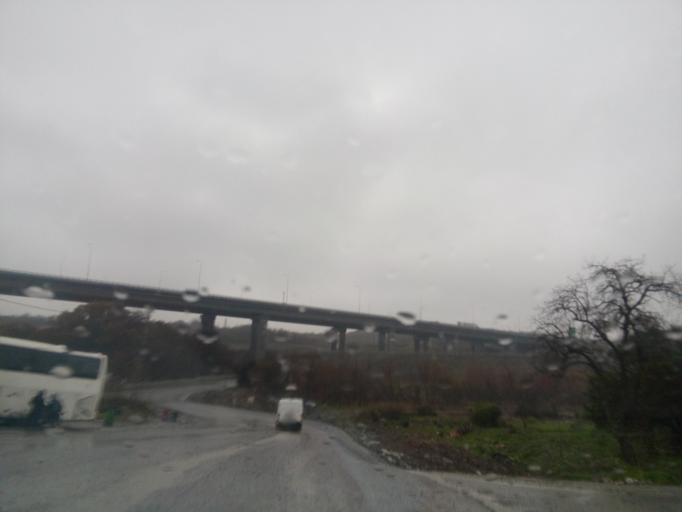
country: TR
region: Istanbul
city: Kemerburgaz
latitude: 41.2398
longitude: 28.8088
